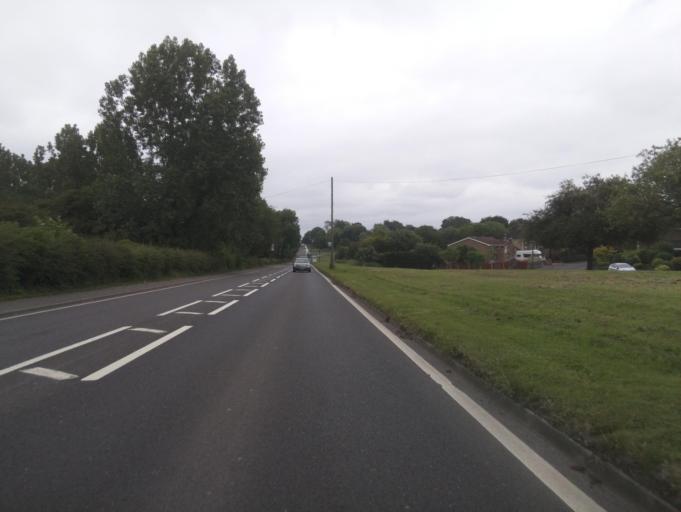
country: GB
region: England
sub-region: Derby
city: Derby
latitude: 52.9316
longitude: -1.5188
